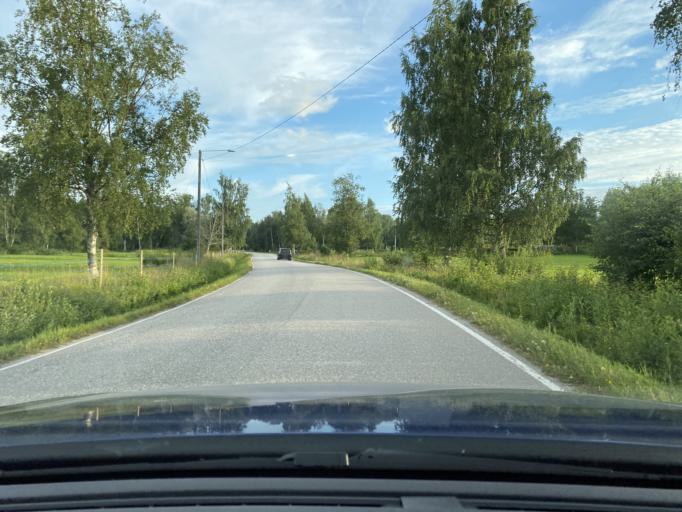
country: FI
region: Ostrobothnia
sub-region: Vaasa
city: Korsnaes
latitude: 62.9627
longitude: 21.1889
